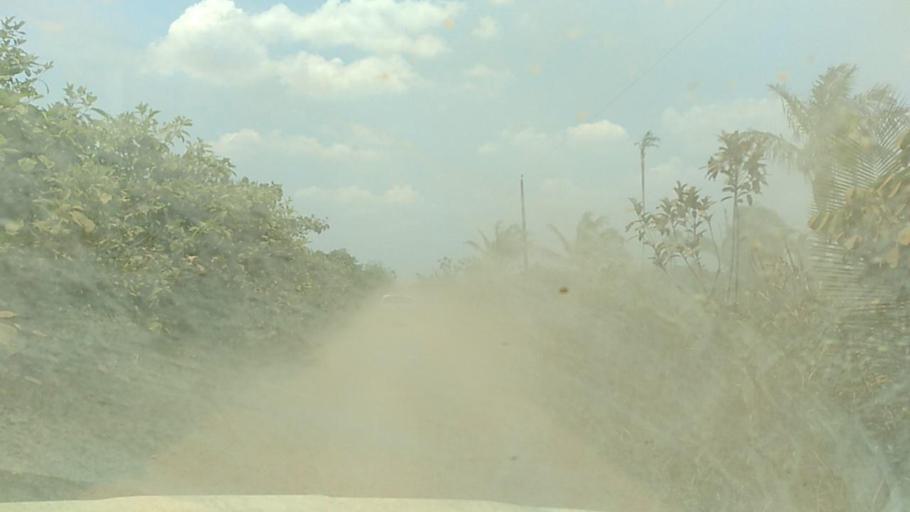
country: BR
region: Rondonia
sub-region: Porto Velho
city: Porto Velho
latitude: -8.7295
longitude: -63.3041
